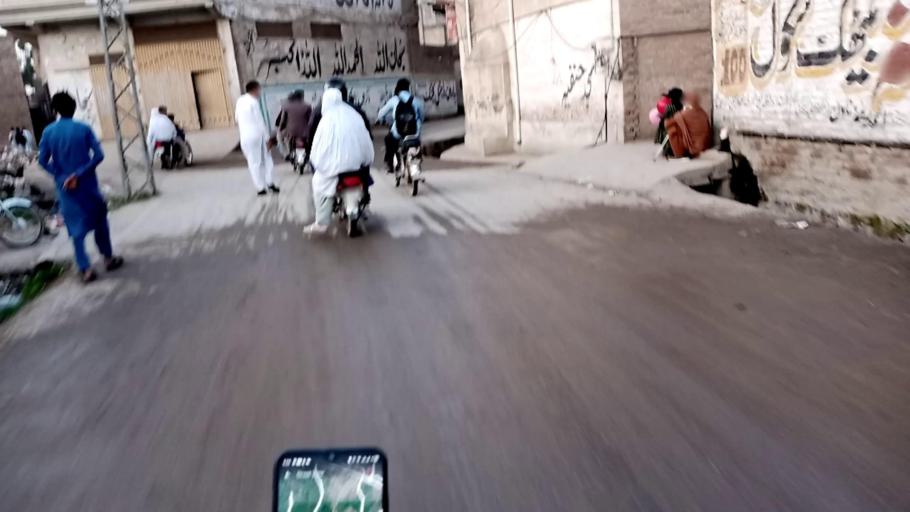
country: PK
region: Khyber Pakhtunkhwa
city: Peshawar
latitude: 34.0286
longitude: 71.4888
